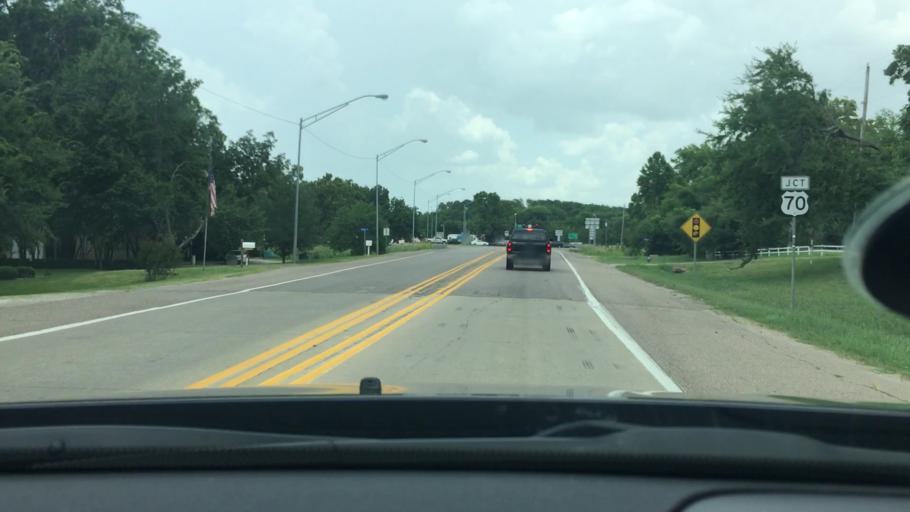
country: US
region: Oklahoma
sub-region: Marshall County
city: Madill
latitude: 34.0821
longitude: -96.7705
